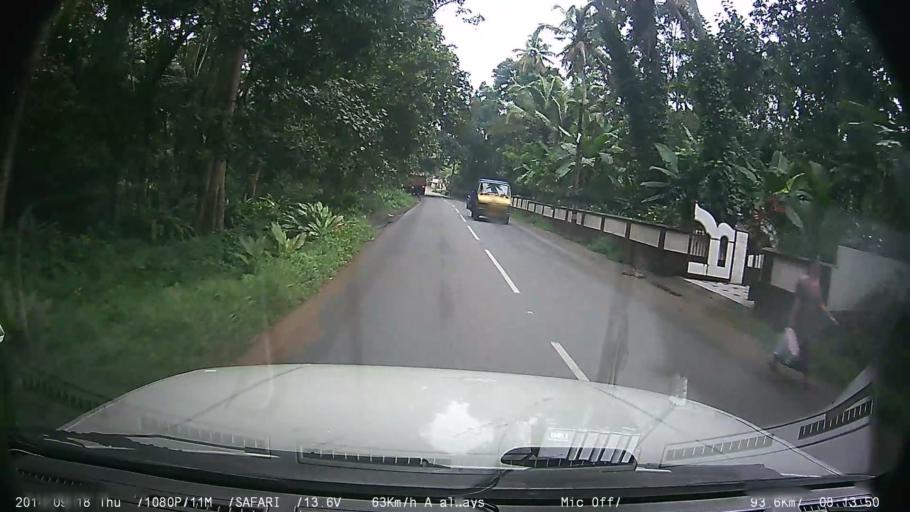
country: IN
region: Kerala
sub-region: Kottayam
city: Kottayam
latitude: 9.6177
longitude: 76.6047
